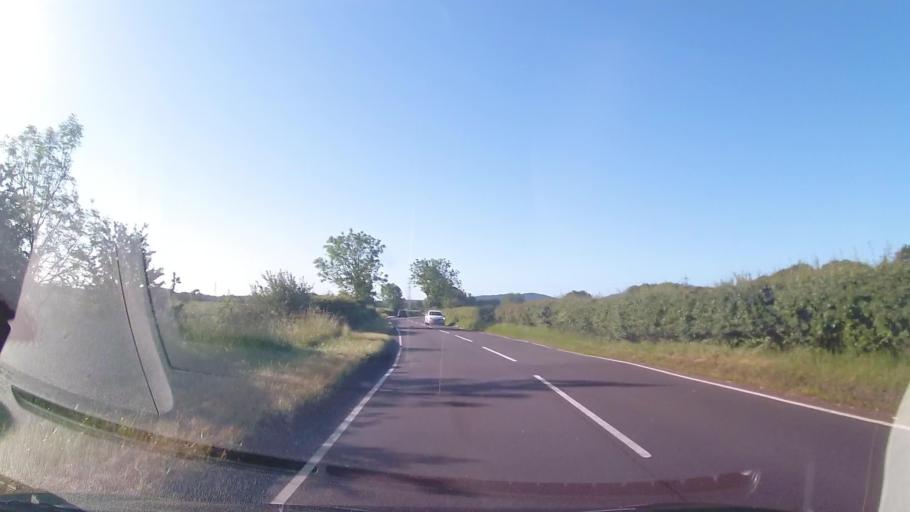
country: GB
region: England
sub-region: Telford and Wrekin
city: Eyton upon the Weald Moors
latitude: 52.7289
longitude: -2.5478
